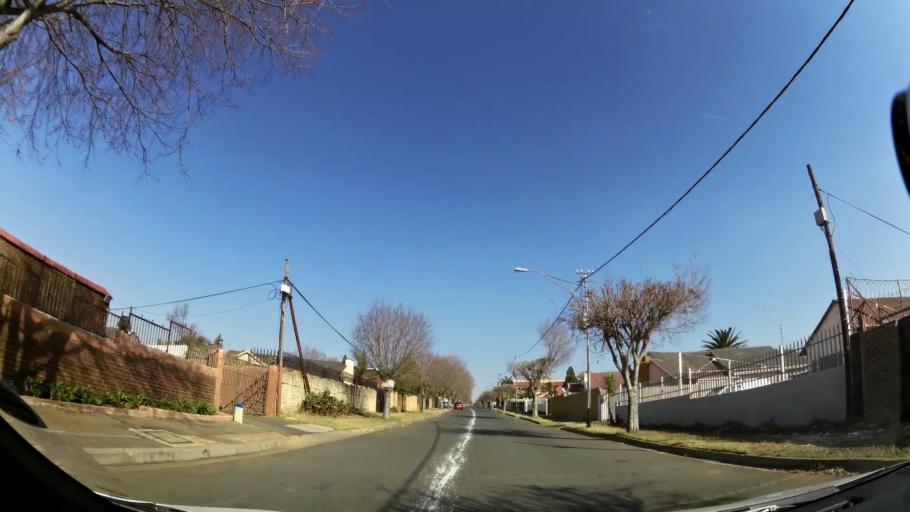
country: ZA
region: Gauteng
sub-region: City of Johannesburg Metropolitan Municipality
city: Johannesburg
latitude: -26.2450
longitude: 28.0078
